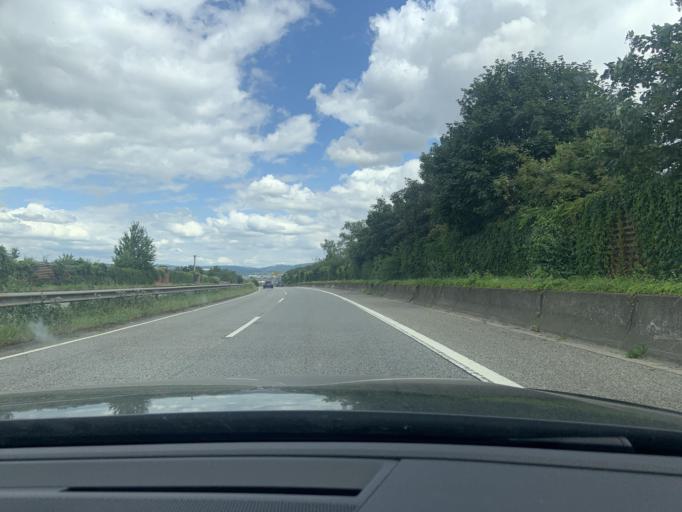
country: DE
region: Rheinland-Pfalz
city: Weissenthurm
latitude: 50.4135
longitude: 7.4450
